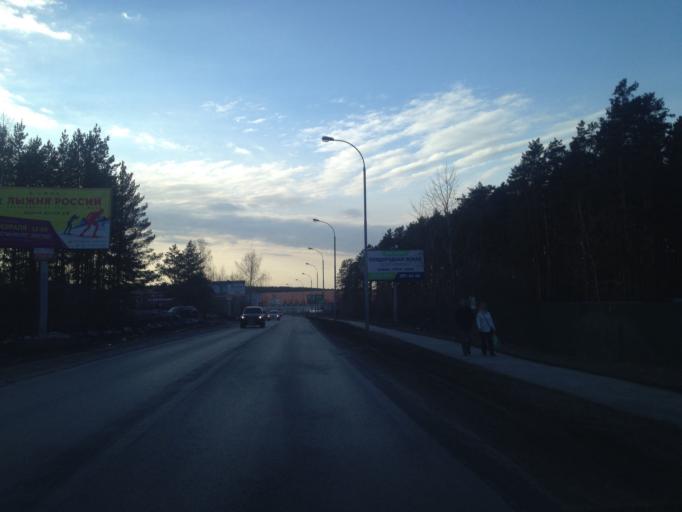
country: RU
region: Sverdlovsk
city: Shirokaya Rechka
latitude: 56.8185
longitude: 60.5111
